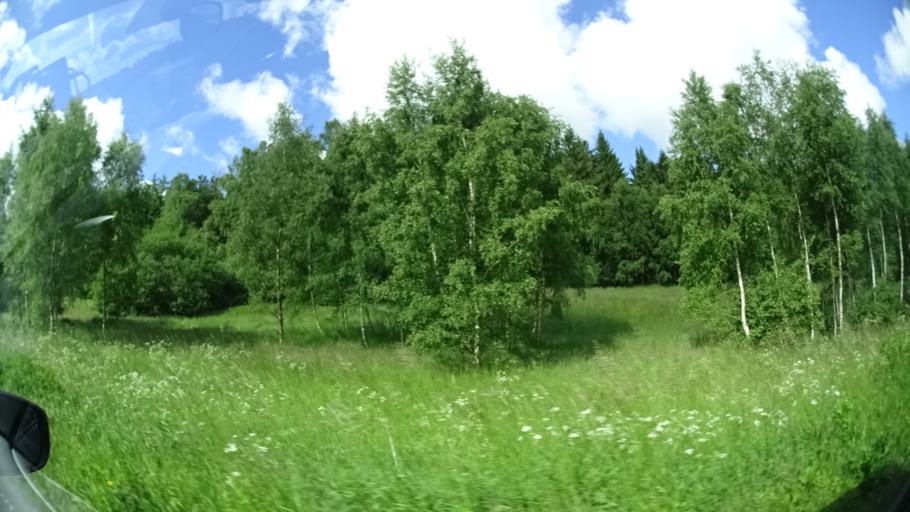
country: DK
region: Central Jutland
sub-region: Syddjurs Kommune
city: Ebeltoft
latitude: 56.2670
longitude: 10.6088
